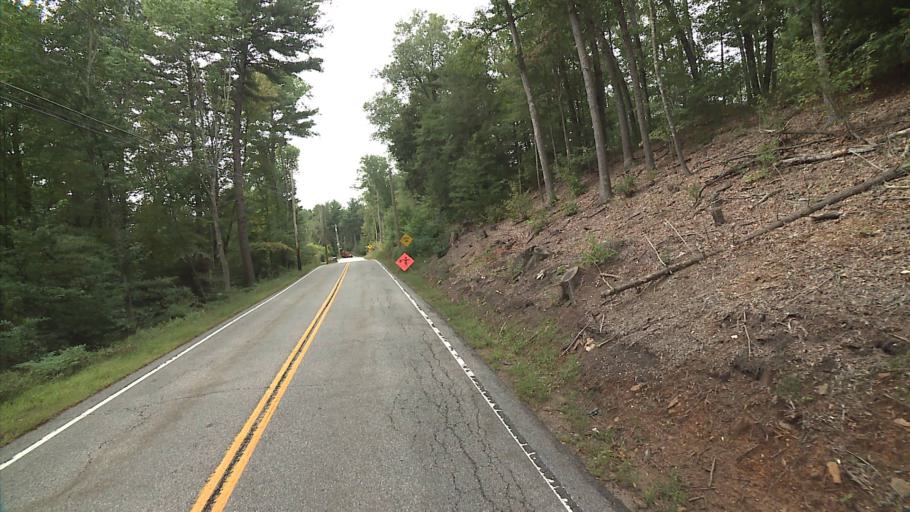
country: US
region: Connecticut
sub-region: Tolland County
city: Stafford Springs
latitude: 41.9046
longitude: -72.2660
